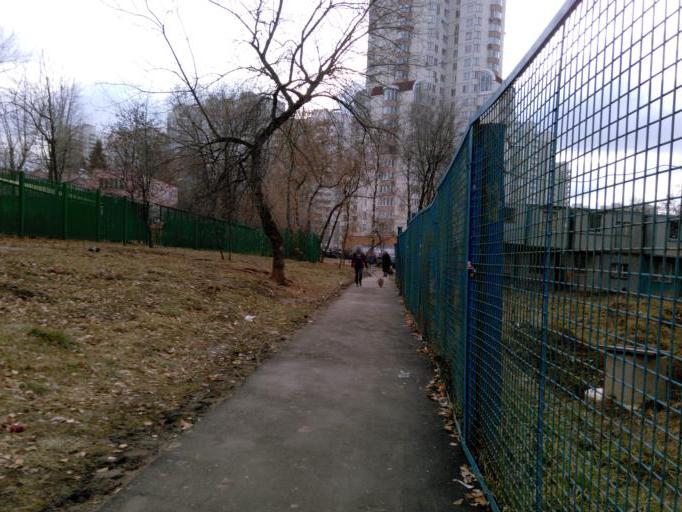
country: RU
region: Moskovskaya
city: Semenovskoye
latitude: 55.6657
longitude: 37.5216
